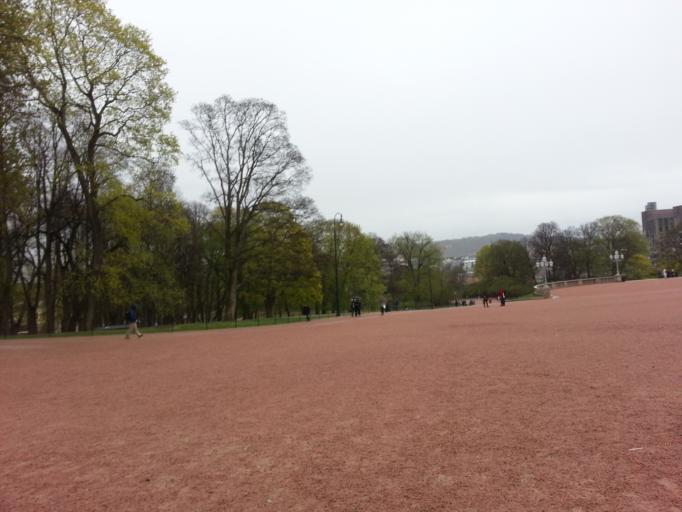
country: NO
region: Oslo
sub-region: Oslo
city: Oslo
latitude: 59.9173
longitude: 10.7286
